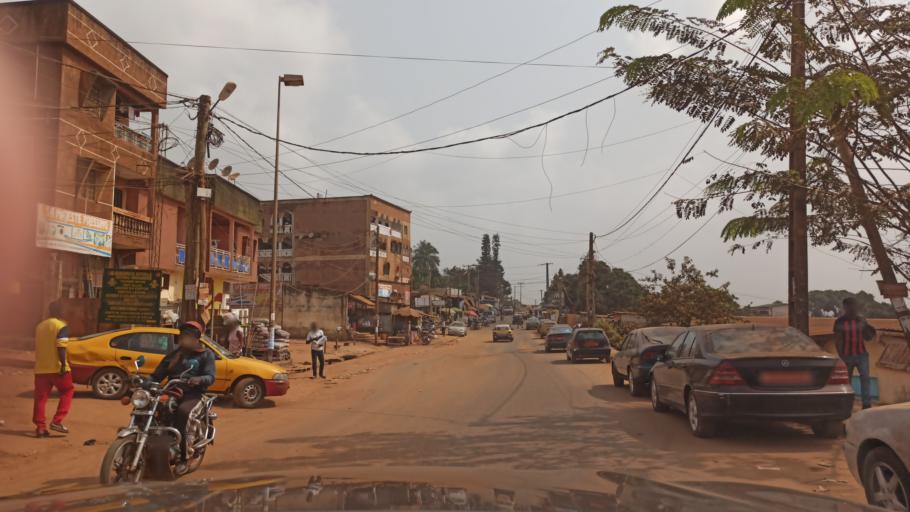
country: CM
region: Centre
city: Yaounde
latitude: 3.8771
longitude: 11.4842
